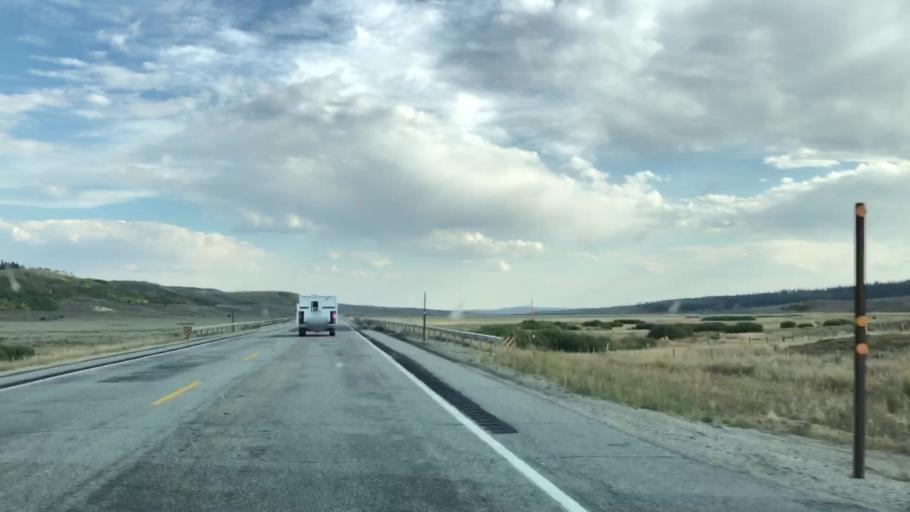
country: US
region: Wyoming
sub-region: Sublette County
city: Pinedale
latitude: 43.1121
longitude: -110.1742
